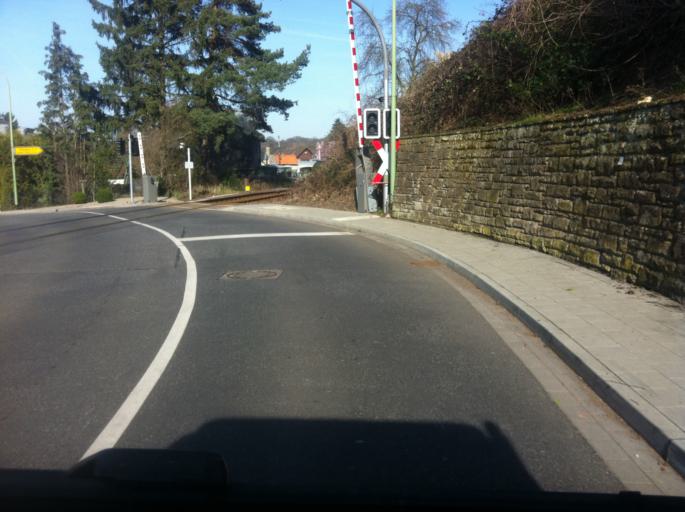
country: DE
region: North Rhine-Westphalia
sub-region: Regierungsbezirk Koln
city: Kreuzau
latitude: 50.7269
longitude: 6.4789
